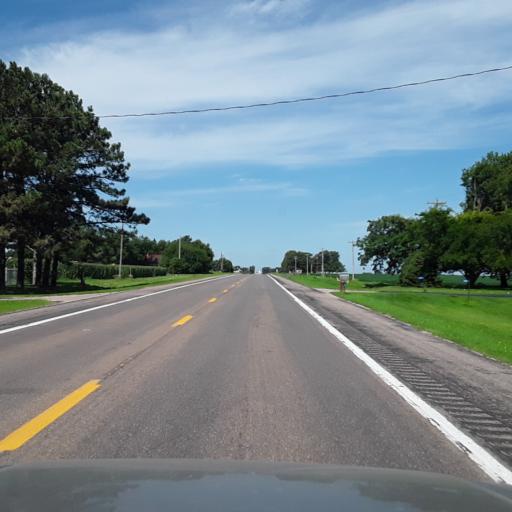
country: US
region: Nebraska
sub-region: Seward County
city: Seward
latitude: 40.9017
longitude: -97.1533
